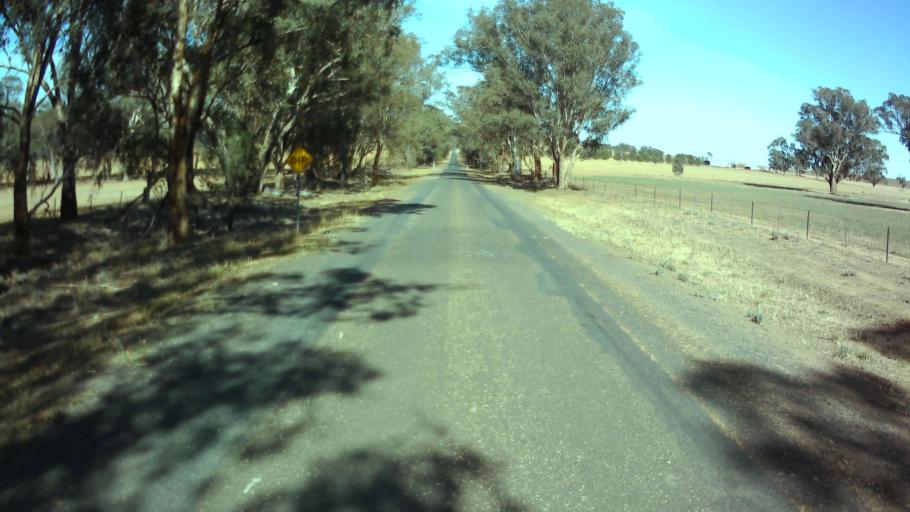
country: AU
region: New South Wales
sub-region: Weddin
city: Grenfell
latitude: -33.9075
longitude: 148.0775
